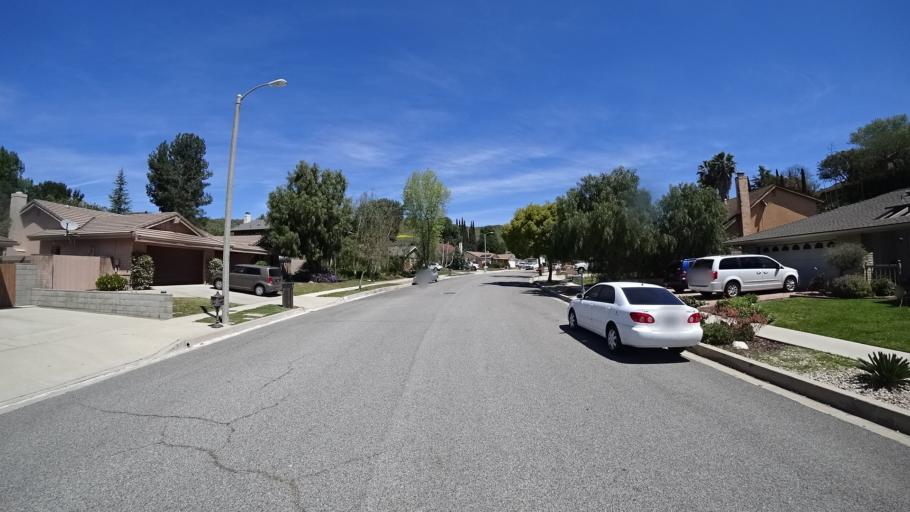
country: US
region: California
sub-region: Ventura County
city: Moorpark
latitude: 34.2315
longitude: -118.8727
